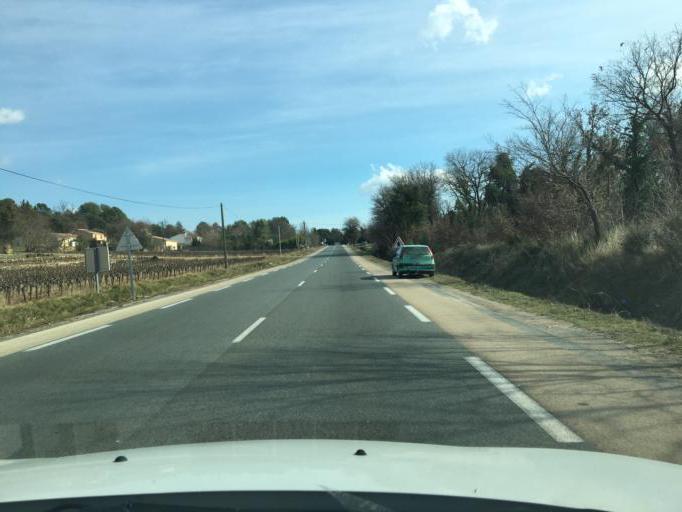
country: FR
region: Provence-Alpes-Cote d'Azur
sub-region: Departement du Var
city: Flayosc
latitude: 43.5322
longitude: 6.4128
